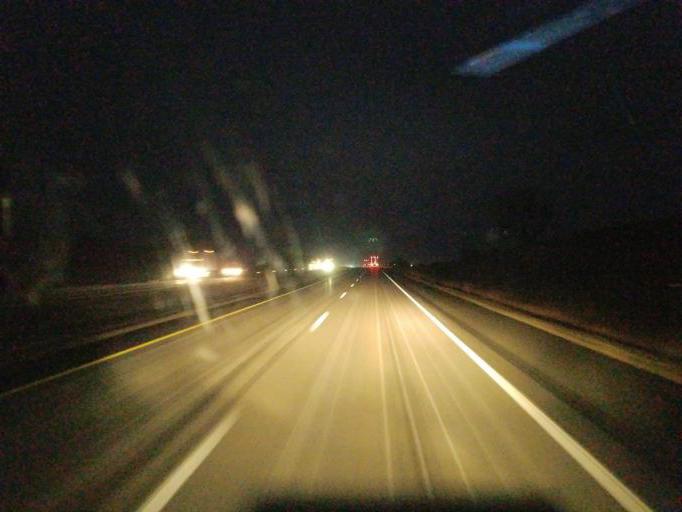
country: US
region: Iowa
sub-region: Guthrie County
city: Stuart
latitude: 41.4959
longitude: -94.3876
